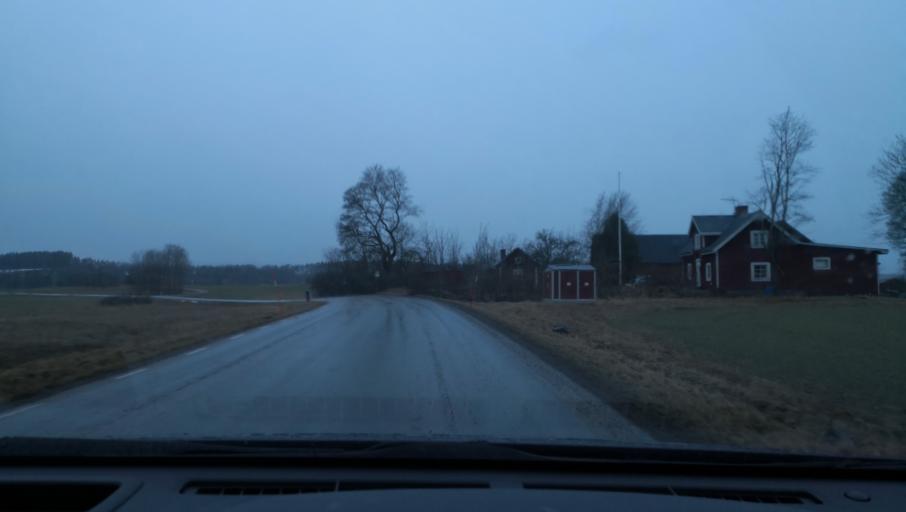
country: SE
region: Soedermanland
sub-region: Eskilstuna Kommun
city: Arla
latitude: 59.4056
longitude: 16.6851
